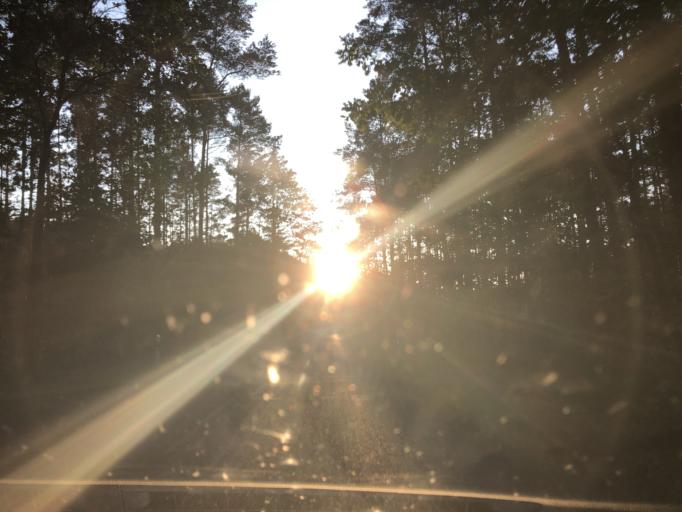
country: DE
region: Brandenburg
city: Mullrose
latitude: 52.2486
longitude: 14.4491
